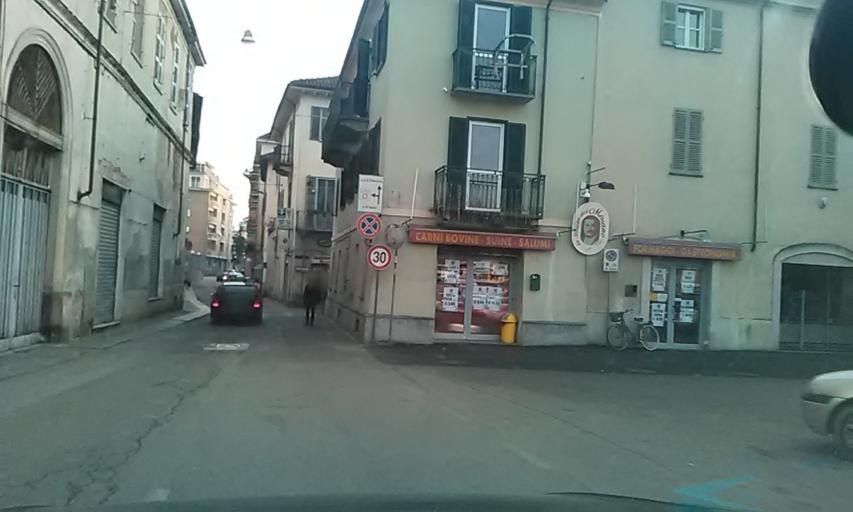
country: IT
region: Piedmont
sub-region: Provincia di Alessandria
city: Casale Monferrato
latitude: 45.1364
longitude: 8.4477
